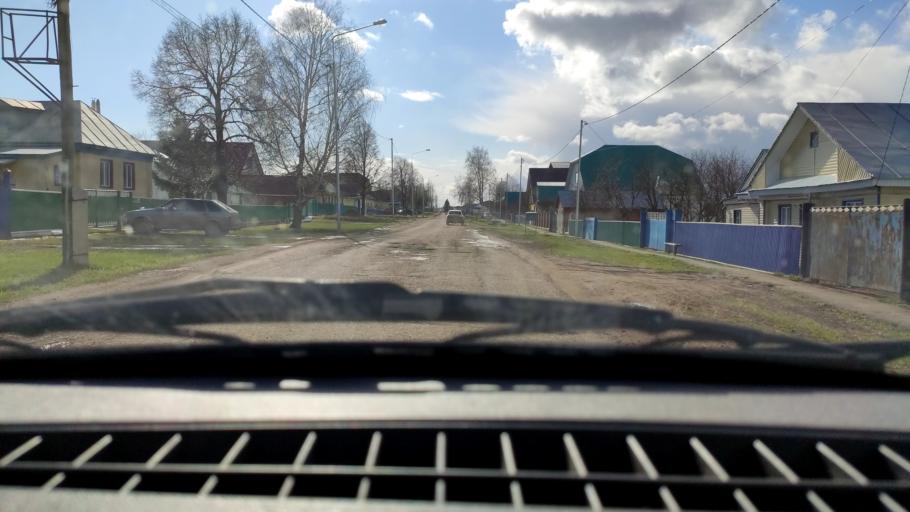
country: RU
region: Bashkortostan
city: Chekmagush
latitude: 55.1320
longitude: 54.6460
